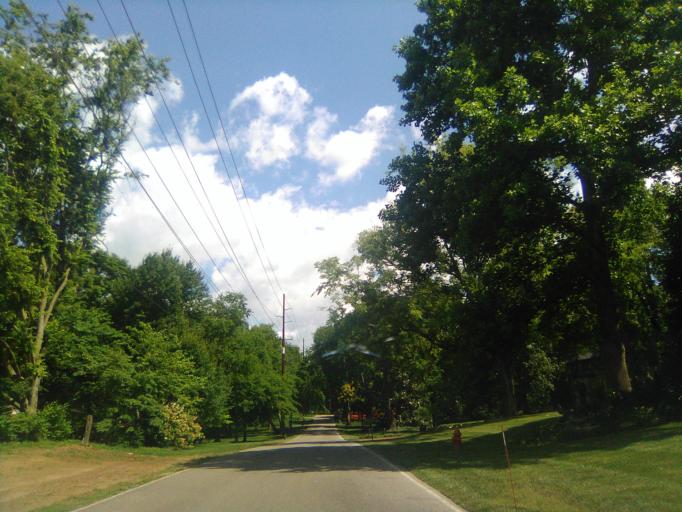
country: US
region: Tennessee
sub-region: Davidson County
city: Belle Meade
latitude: 36.0997
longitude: -86.8591
